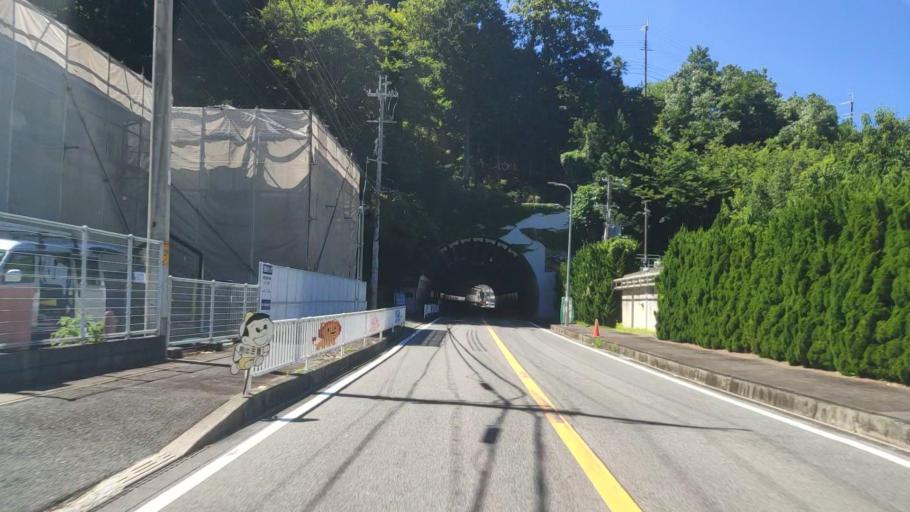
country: JP
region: Nara
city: Yoshino-cho
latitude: 34.3355
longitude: 135.9557
